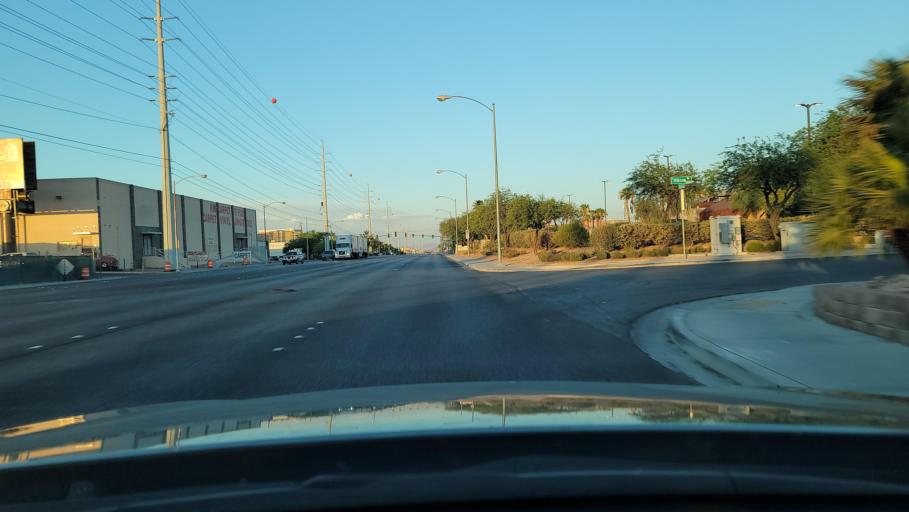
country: US
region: Nevada
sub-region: Clark County
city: Spring Valley
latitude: 36.0862
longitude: -115.2065
